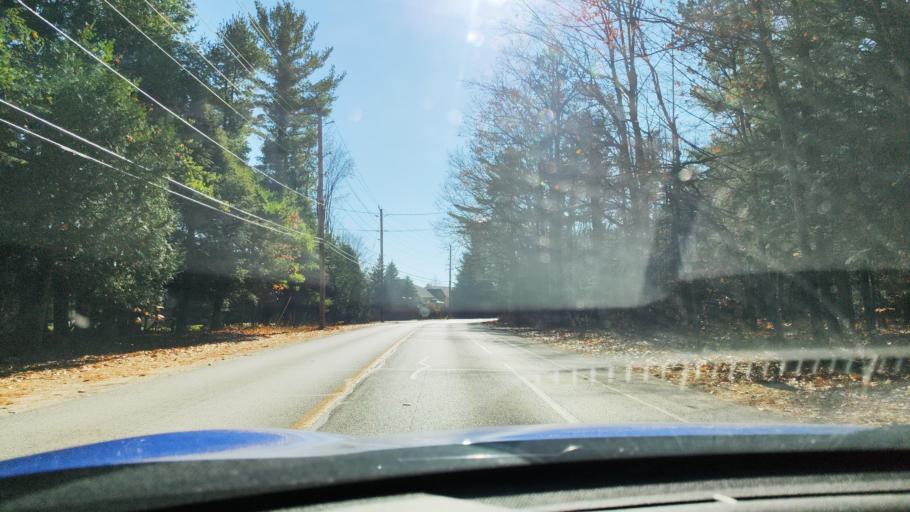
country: CA
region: Ontario
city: Wasaga Beach
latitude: 44.5137
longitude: -79.9952
